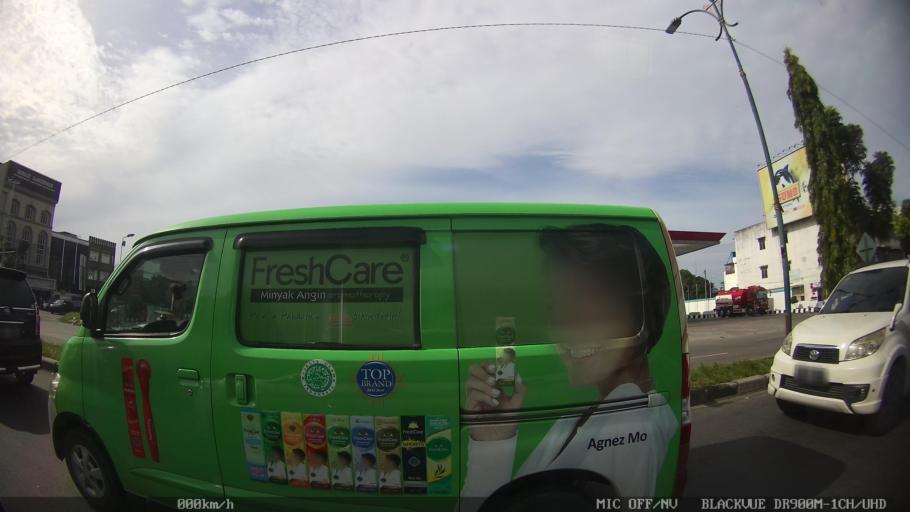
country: ID
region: North Sumatra
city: Medan
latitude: 3.6298
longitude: 98.6805
